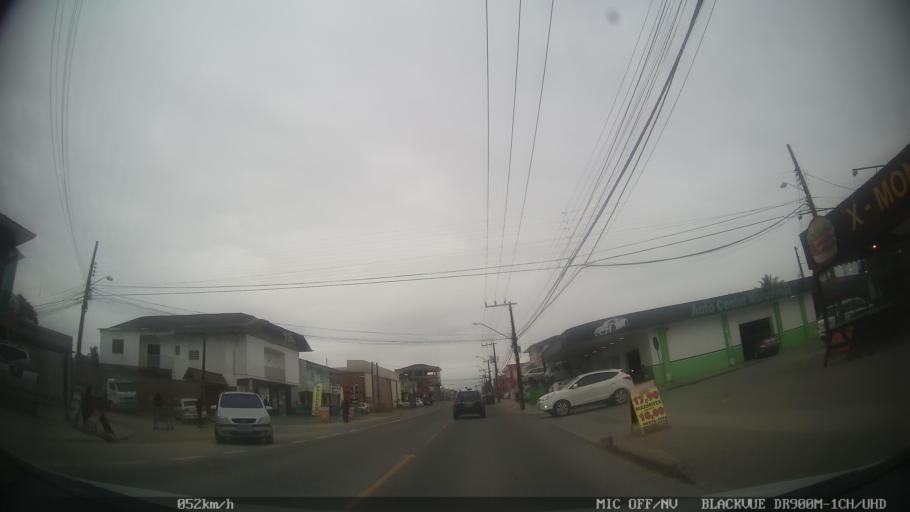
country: BR
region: Santa Catarina
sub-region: Joinville
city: Joinville
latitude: -26.3235
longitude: -48.8173
